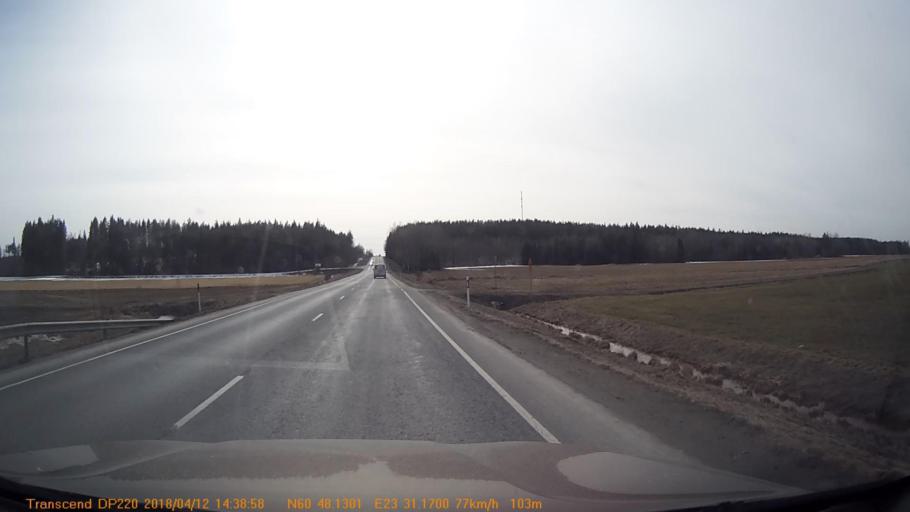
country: FI
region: Haeme
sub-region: Forssa
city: Jokioinen
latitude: 60.8012
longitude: 23.5177
